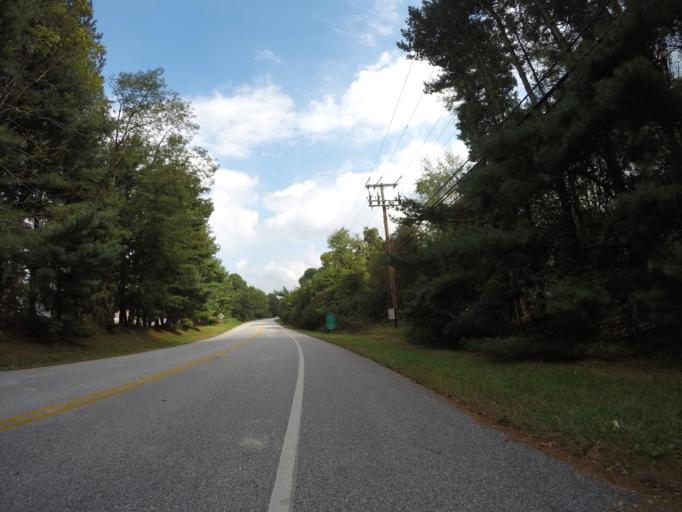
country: US
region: Maryland
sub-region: Howard County
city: Columbia
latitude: 39.2564
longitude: -76.8642
